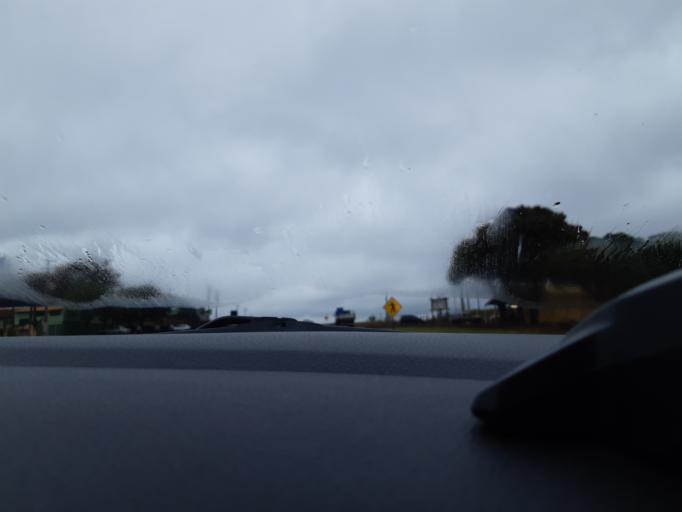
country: BR
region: Parana
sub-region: Bandeirantes
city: Bandeirantes
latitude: -23.0548
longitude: -50.2432
